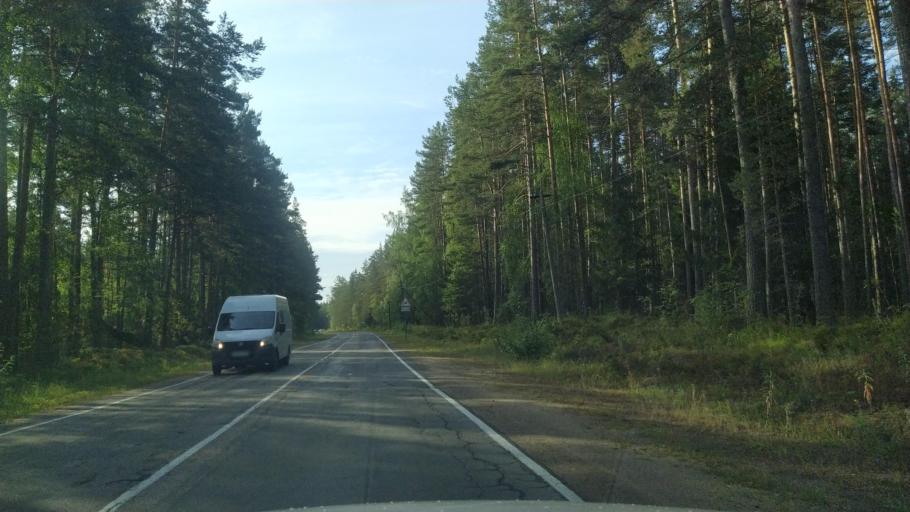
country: RU
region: Leningrad
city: Priozersk
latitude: 60.9976
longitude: 30.2490
